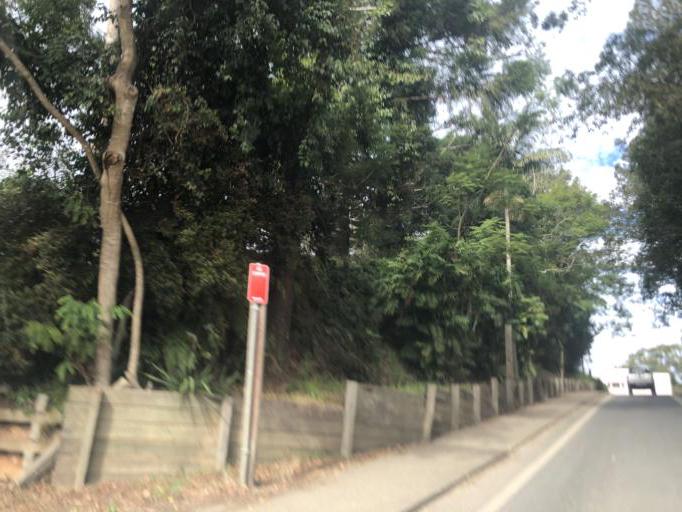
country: AU
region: New South Wales
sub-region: Bellingen
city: Bellingen
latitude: -30.4512
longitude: 152.8983
